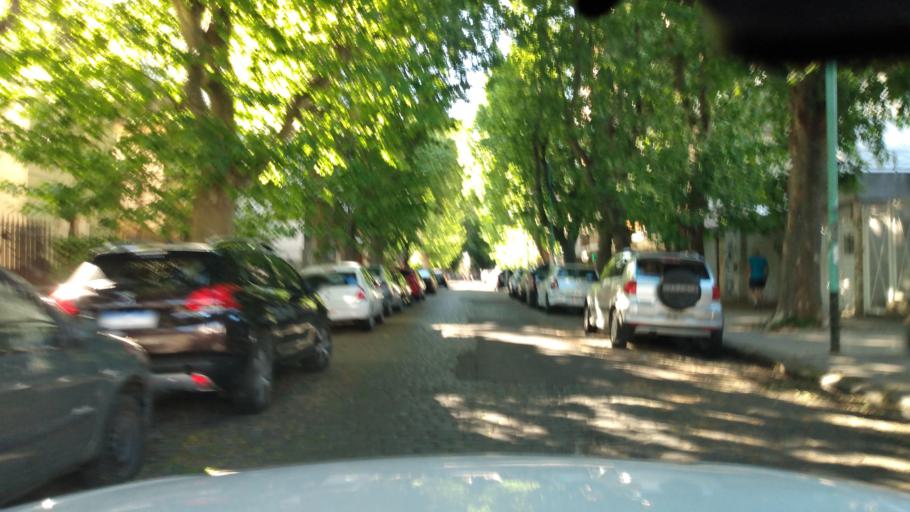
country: AR
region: Buenos Aires F.D.
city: Villa Santa Rita
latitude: -34.5805
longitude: -58.4867
